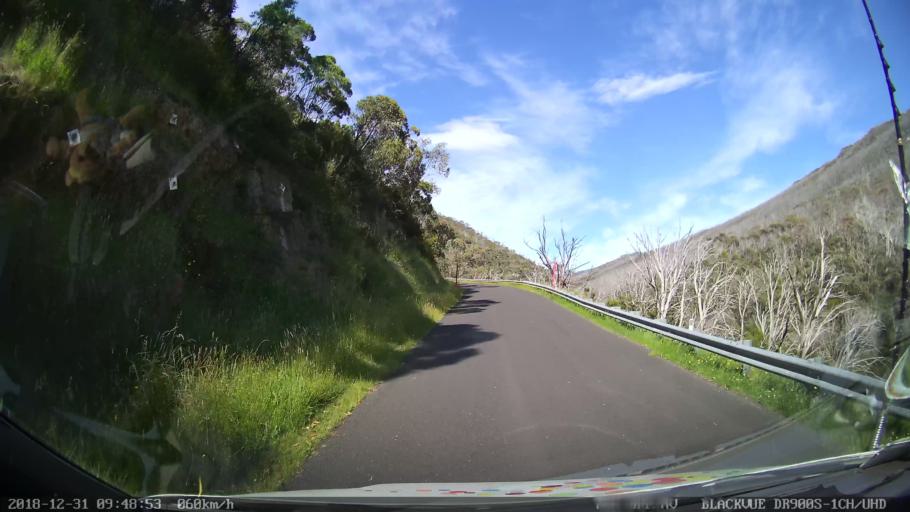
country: AU
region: New South Wales
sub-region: Snowy River
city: Jindabyne
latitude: -36.5147
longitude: 148.2880
